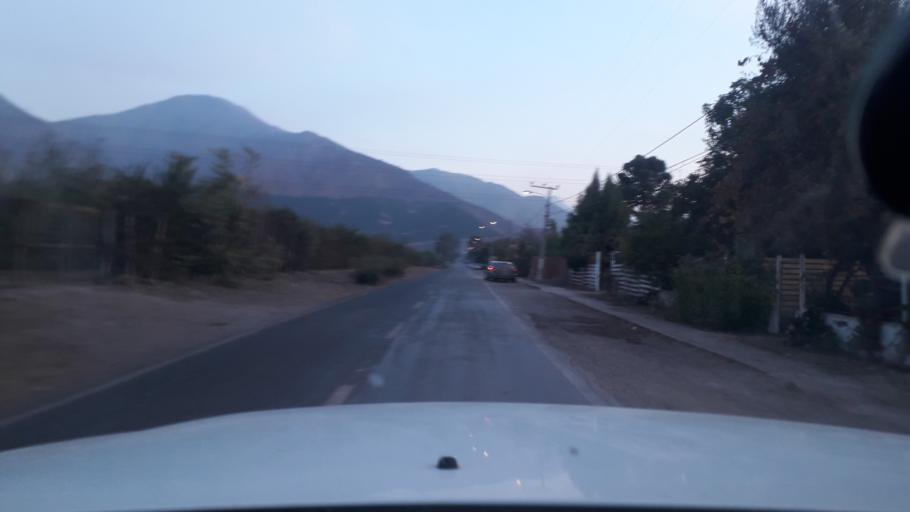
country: CL
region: Valparaiso
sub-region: Provincia de San Felipe
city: Llaillay
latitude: -32.8222
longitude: -71.0283
